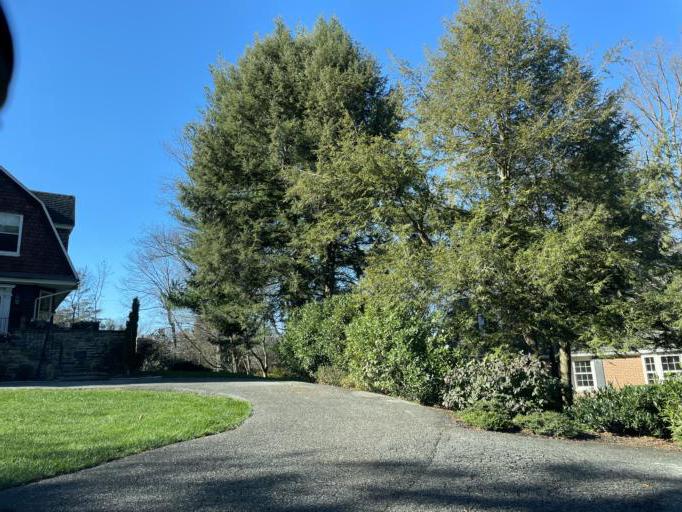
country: US
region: Maryland
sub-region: Baltimore County
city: Mays Chapel
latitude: 39.4025
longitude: -76.6564
